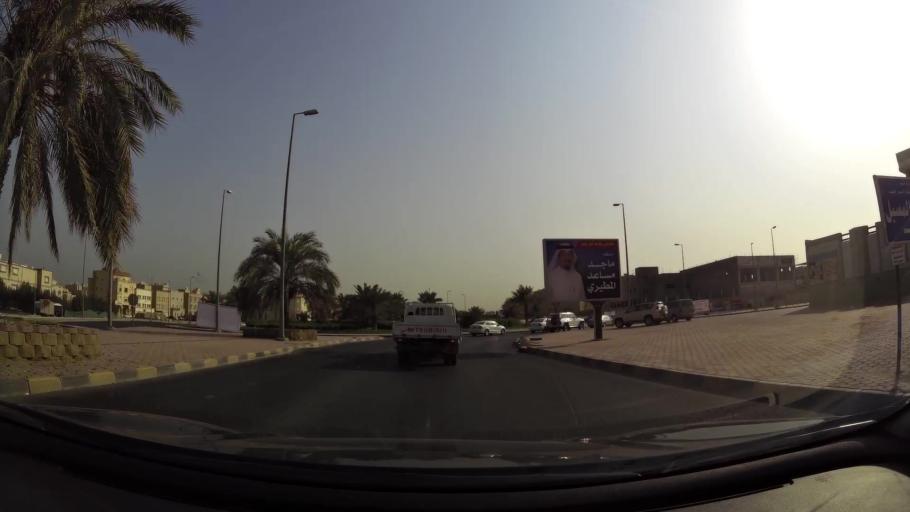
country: KW
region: Al Ahmadi
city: Ar Riqqah
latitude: 29.1279
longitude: 48.1040
